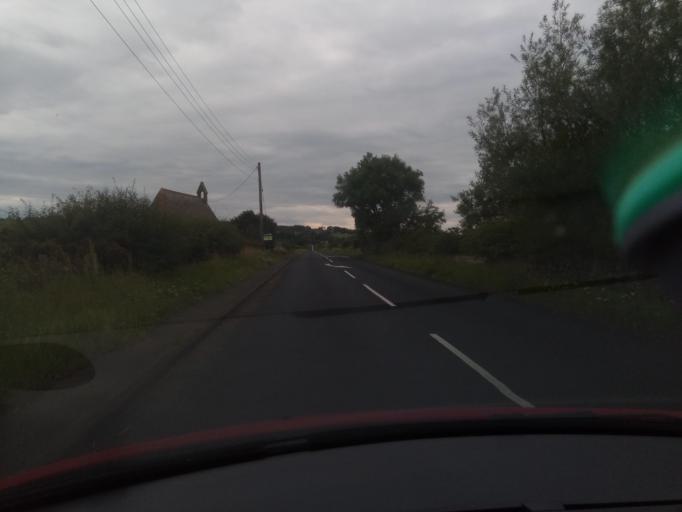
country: GB
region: England
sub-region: Northumberland
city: Warden
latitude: 54.9680
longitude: -2.1545
